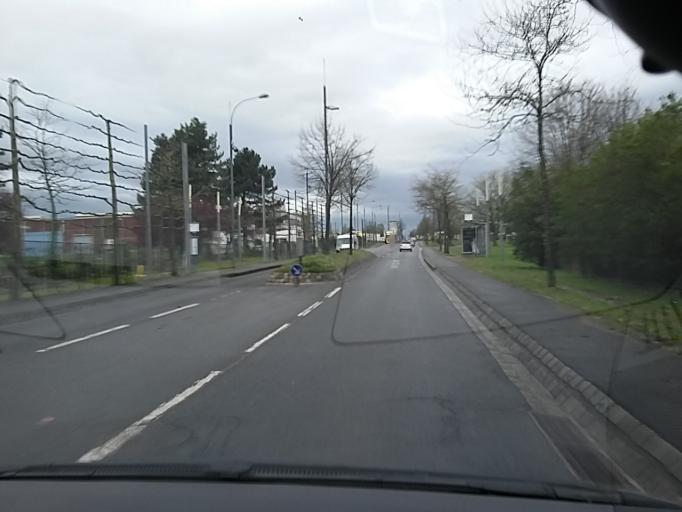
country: FR
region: Picardie
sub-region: Departement de la Somme
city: Amiens
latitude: 49.9304
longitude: 2.2790
